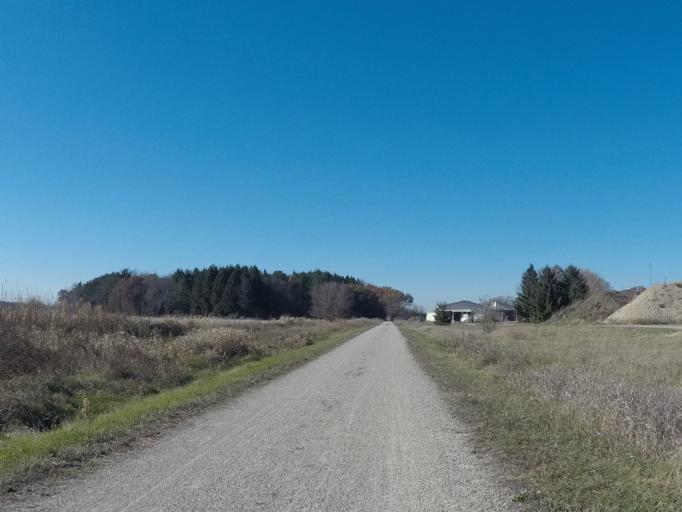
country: US
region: Wisconsin
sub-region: Jefferson County
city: Lake Mills
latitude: 43.0648
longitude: -88.9579
